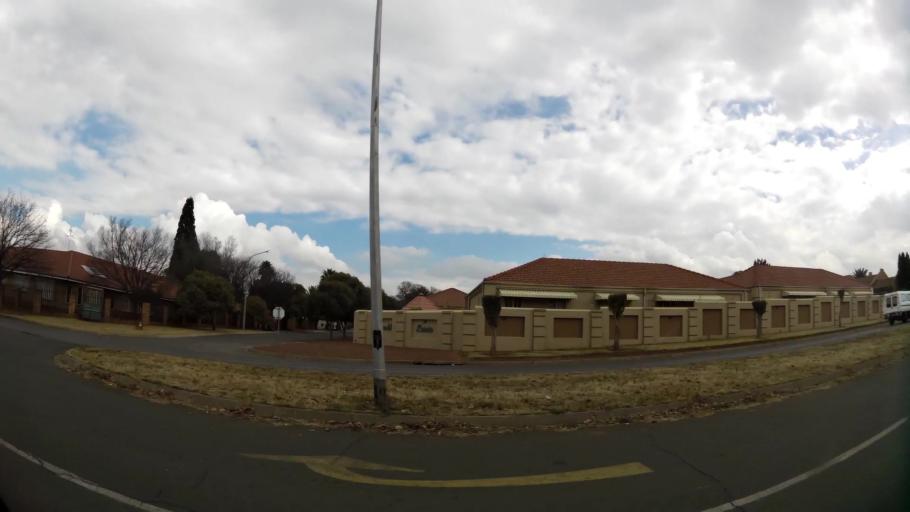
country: ZA
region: Gauteng
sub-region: Sedibeng District Municipality
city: Vanderbijlpark
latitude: -26.7326
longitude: 27.8540
